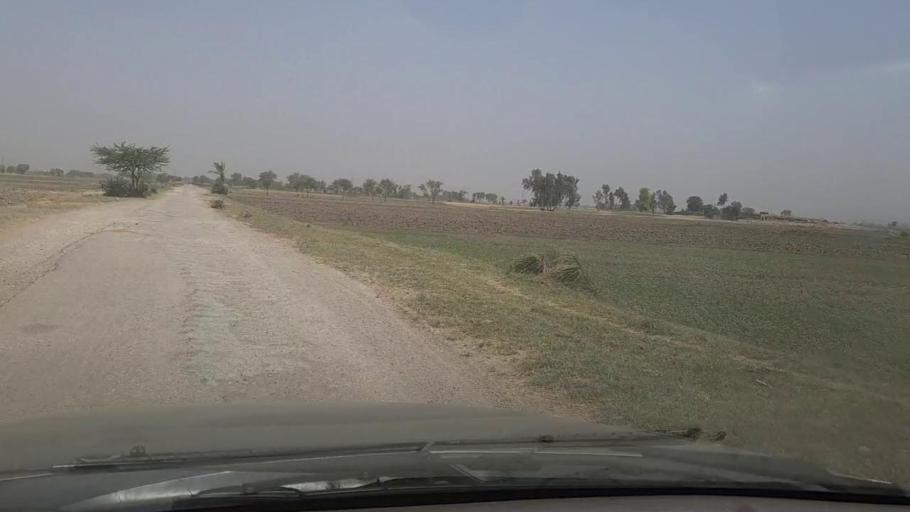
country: PK
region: Sindh
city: Madeji
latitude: 27.8180
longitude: 68.3974
